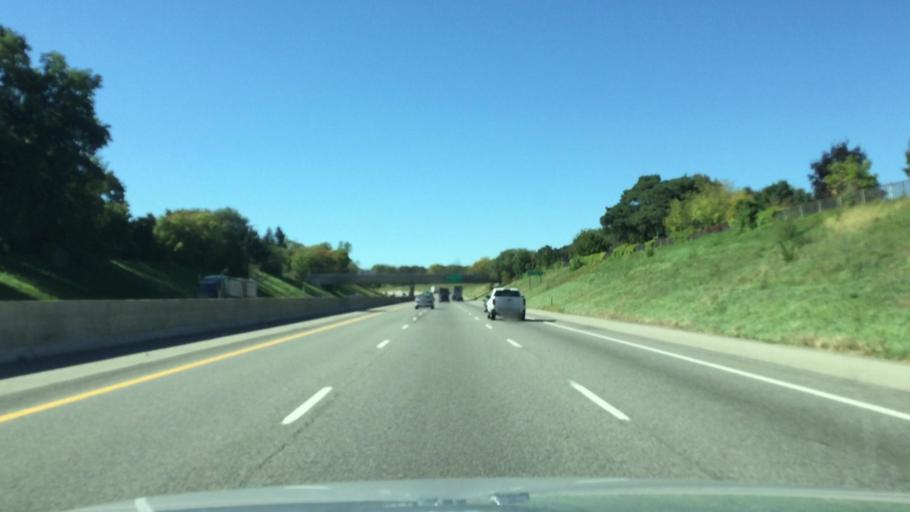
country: US
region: Michigan
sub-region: Wayne County
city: Plymouth
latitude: 42.3884
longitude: -83.4528
